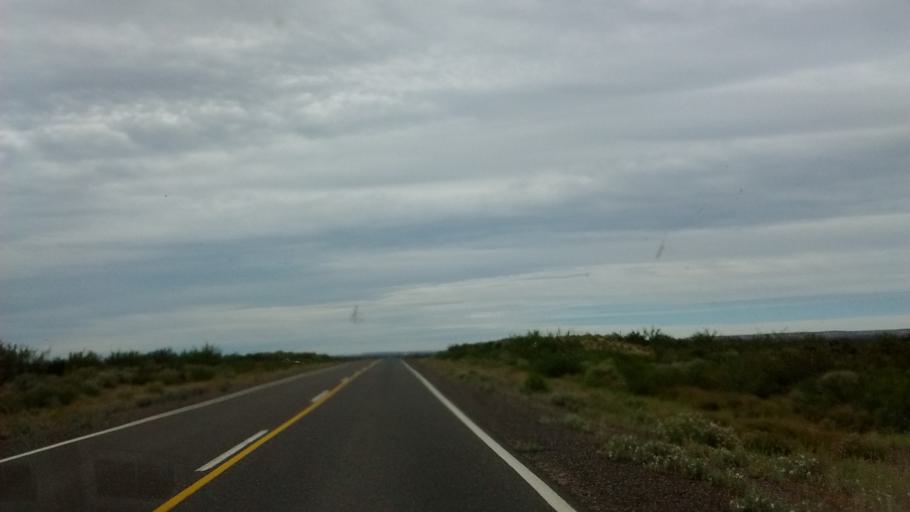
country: AR
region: Rio Negro
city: Catriel
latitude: -38.0840
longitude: -67.9253
